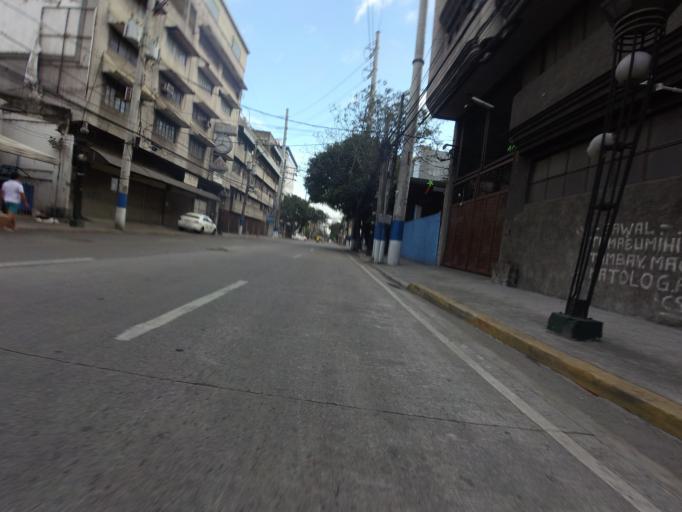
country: PH
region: Metro Manila
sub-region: City of Manila
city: Quiapo
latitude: 14.5789
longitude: 120.9894
